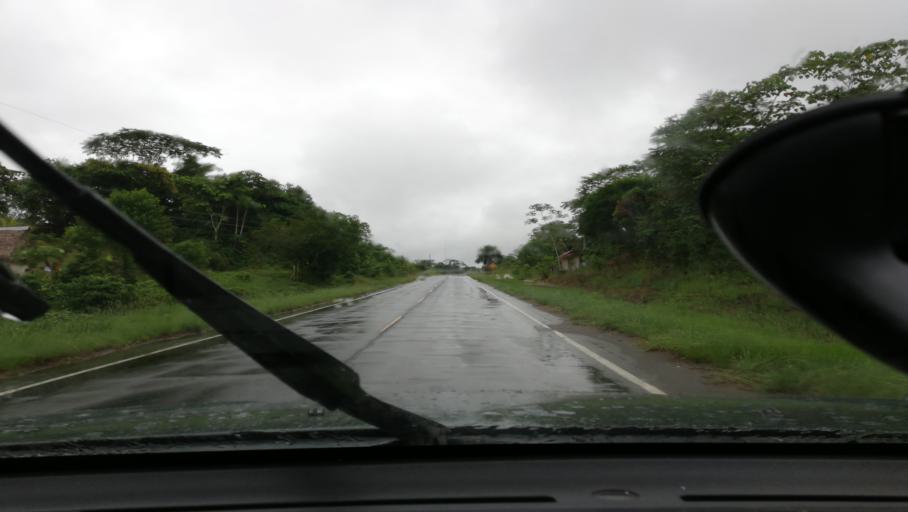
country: PE
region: Loreto
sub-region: Provincia de Maynas
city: San Juan
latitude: -4.1648
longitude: -73.4741
